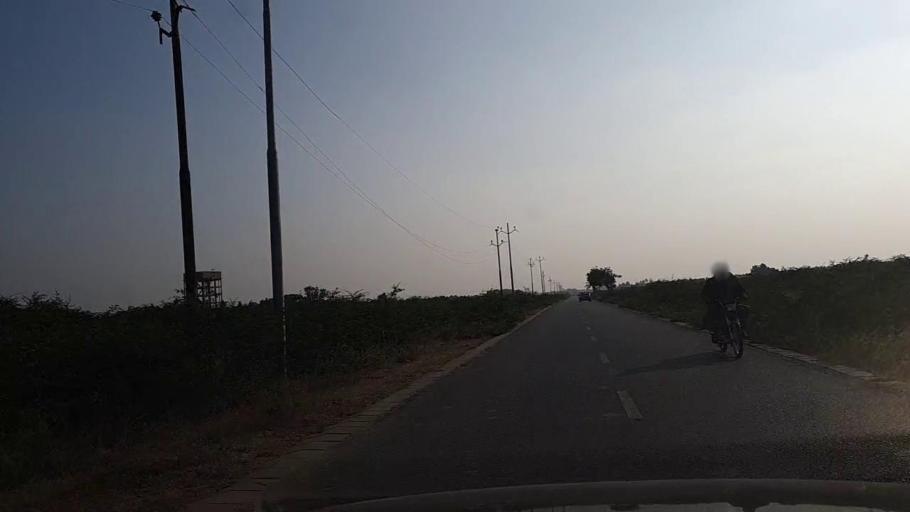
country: PK
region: Sindh
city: Gharo
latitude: 24.7932
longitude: 67.5170
